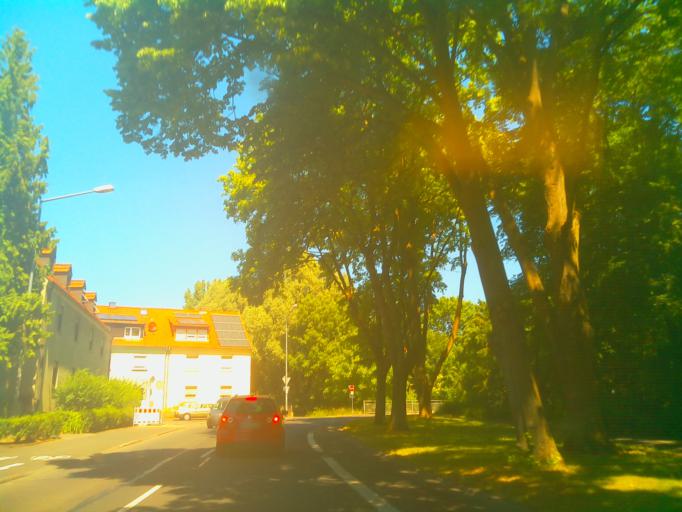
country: DE
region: Bavaria
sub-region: Regierungsbezirk Unterfranken
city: Schweinfurt
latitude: 50.0554
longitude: 10.2313
